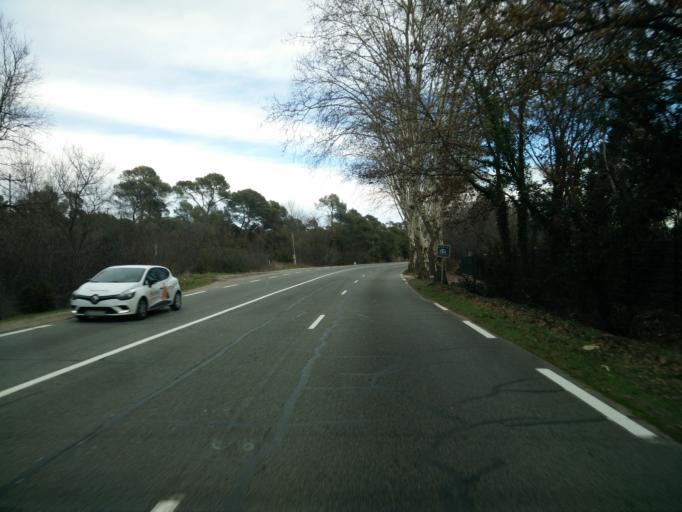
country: FR
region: Provence-Alpes-Cote d'Azur
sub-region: Departement du Var
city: Roquebrune-sur-Argens
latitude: 43.4674
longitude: 6.6079
